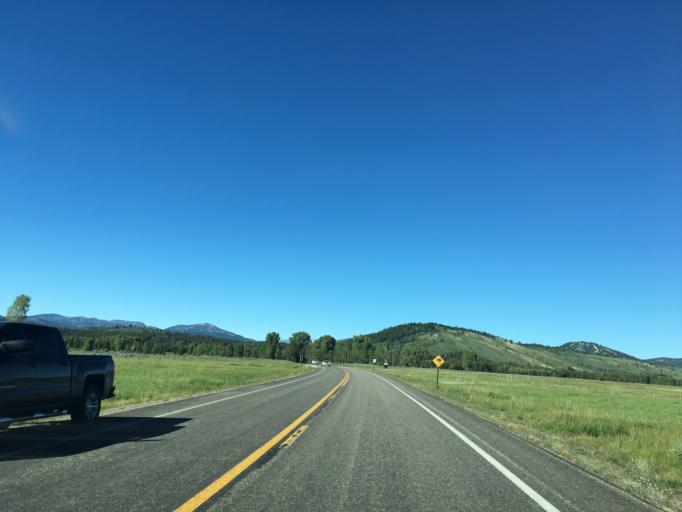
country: US
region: Wyoming
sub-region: Teton County
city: Jackson
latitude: 43.8258
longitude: -110.5162
